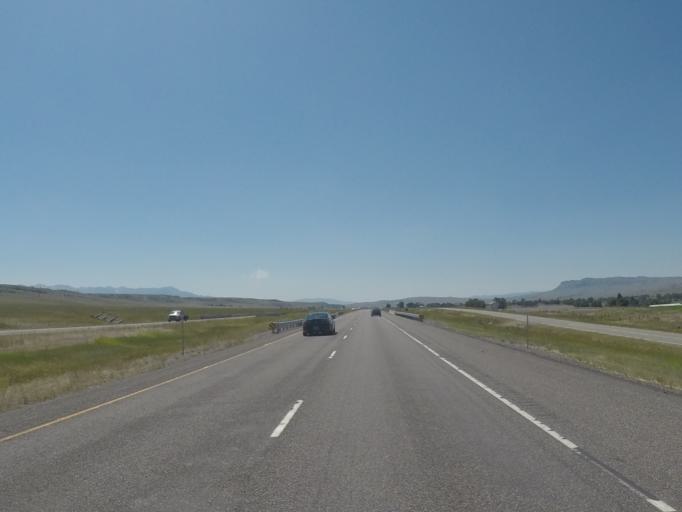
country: US
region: Montana
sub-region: Sweet Grass County
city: Big Timber
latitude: 45.7570
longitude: -110.1313
